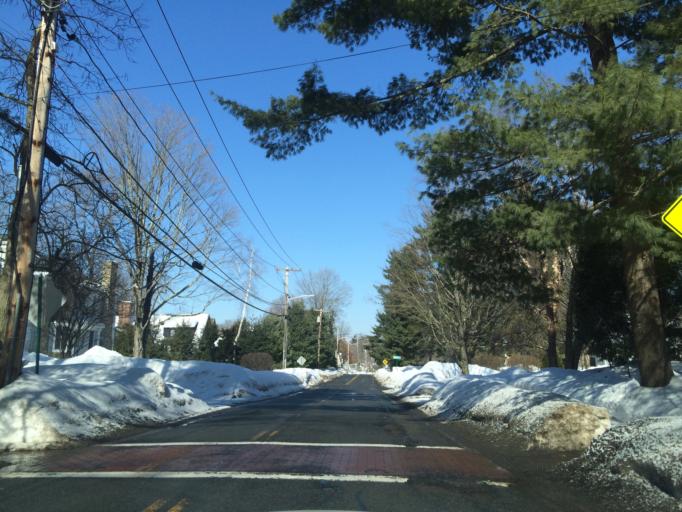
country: US
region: Massachusetts
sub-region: Norfolk County
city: Wellesley
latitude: 42.2852
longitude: -71.2886
